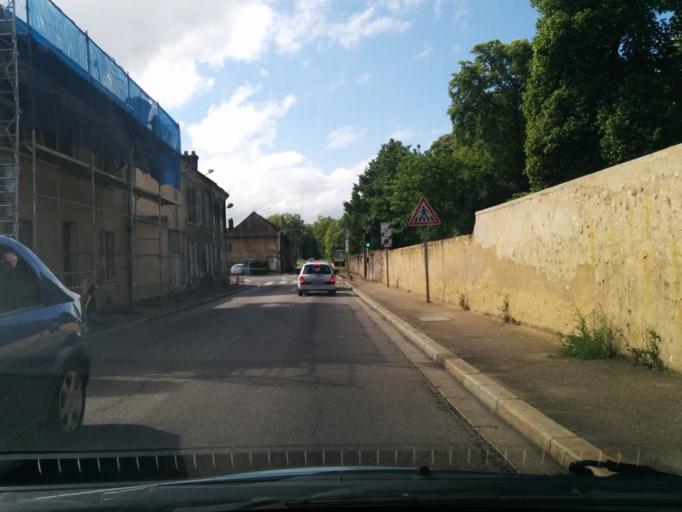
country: FR
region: Ile-de-France
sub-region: Departement des Yvelines
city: Rosny-sur-Seine
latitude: 49.0014
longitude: 1.6301
